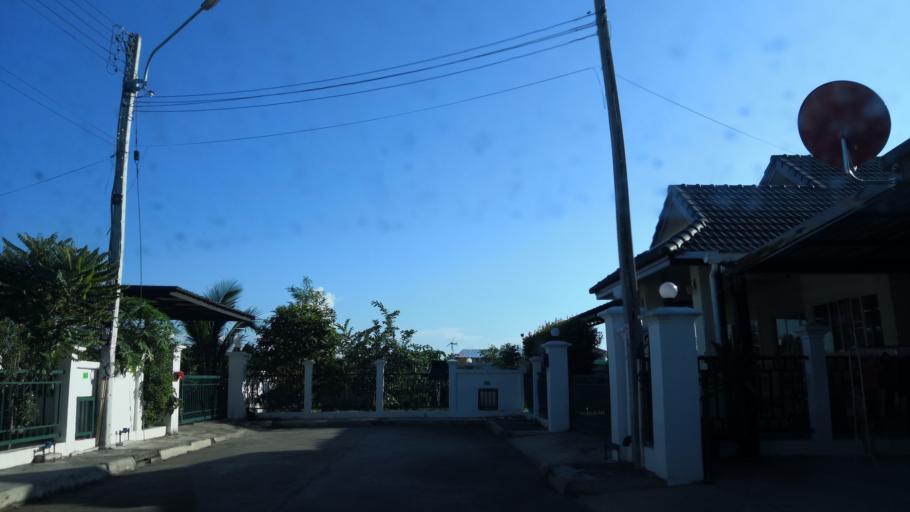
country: TH
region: Chiang Mai
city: Hang Dong
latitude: 18.7178
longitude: 98.9602
